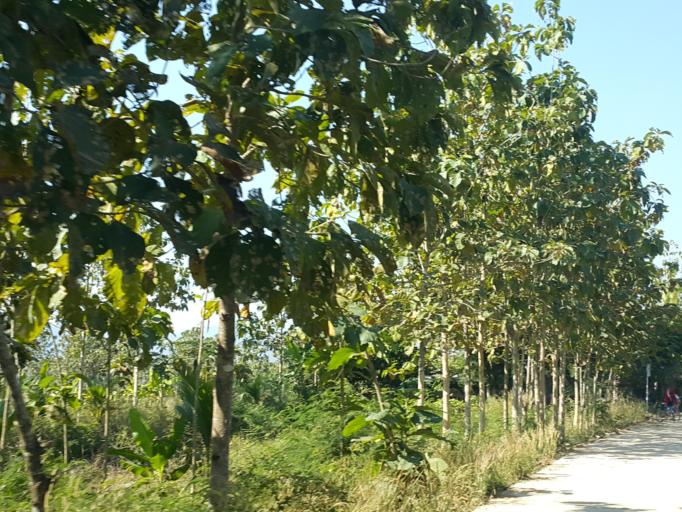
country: TH
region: Sukhothai
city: Thung Saliam
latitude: 17.3410
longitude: 99.4446
